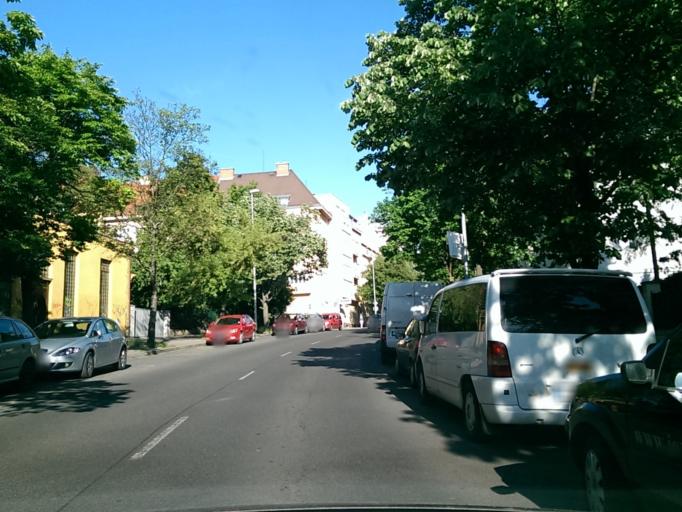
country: CZ
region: Praha
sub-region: Praha 2
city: Vysehrad
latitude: 50.0576
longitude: 14.4275
